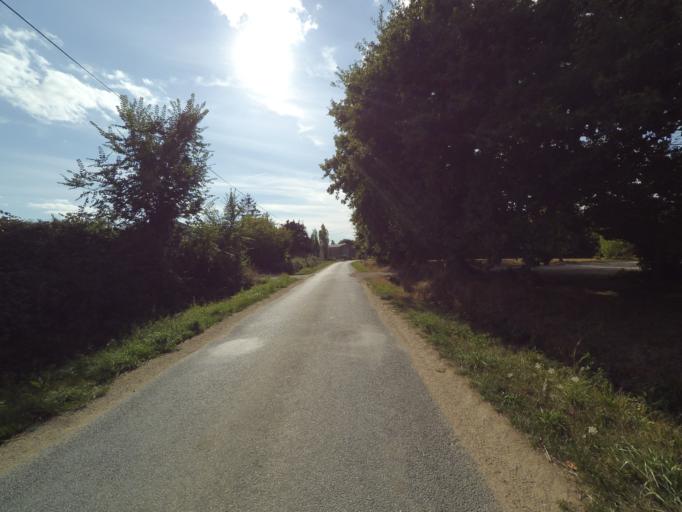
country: FR
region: Pays de la Loire
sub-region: Departement de la Loire-Atlantique
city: Vieillevigne
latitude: 46.9856
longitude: -1.3951
